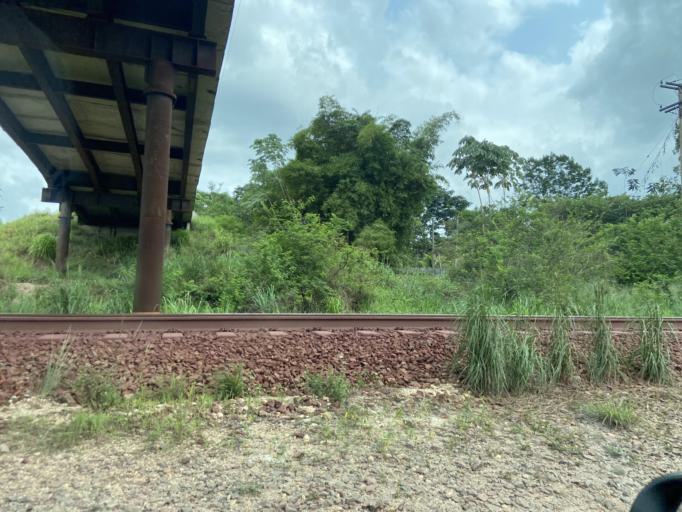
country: BR
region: Para
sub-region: Maraba
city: Maraba
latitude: -5.2884
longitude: -49.0542
